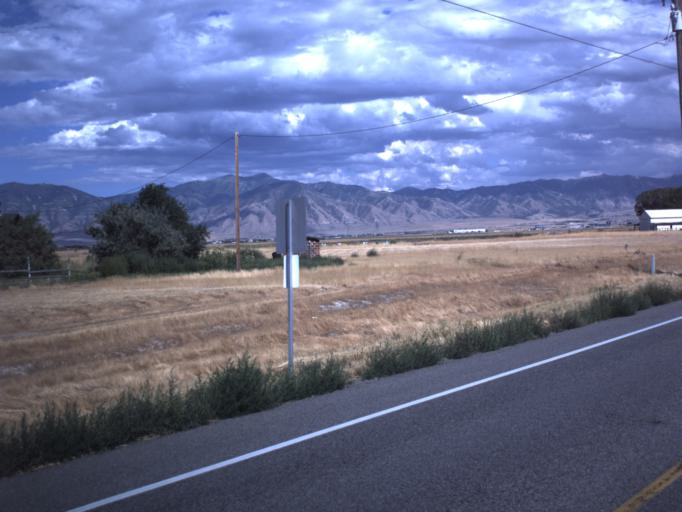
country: US
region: Utah
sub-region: Tooele County
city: Grantsville
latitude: 40.5909
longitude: -112.4206
